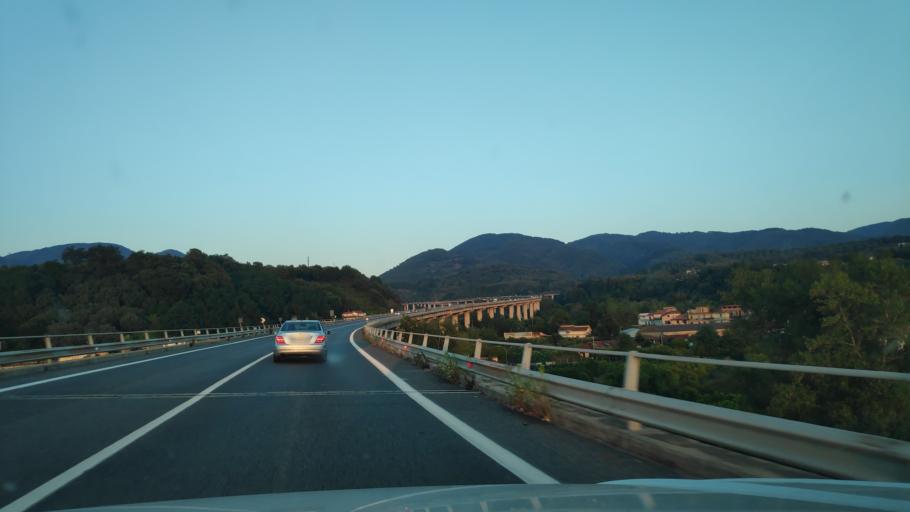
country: IT
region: Calabria
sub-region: Provincia di Reggio Calabria
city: Anoia Superiore
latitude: 38.4216
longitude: 16.0961
